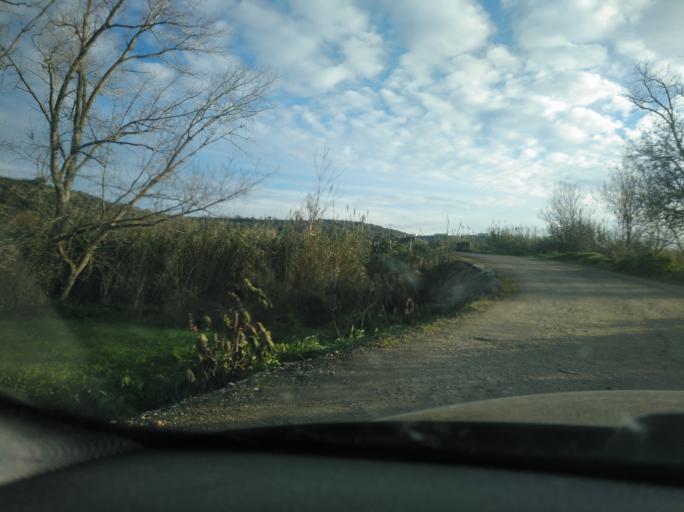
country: PT
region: Lisbon
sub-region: Loures
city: Apelacao
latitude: 38.8299
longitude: -9.1435
